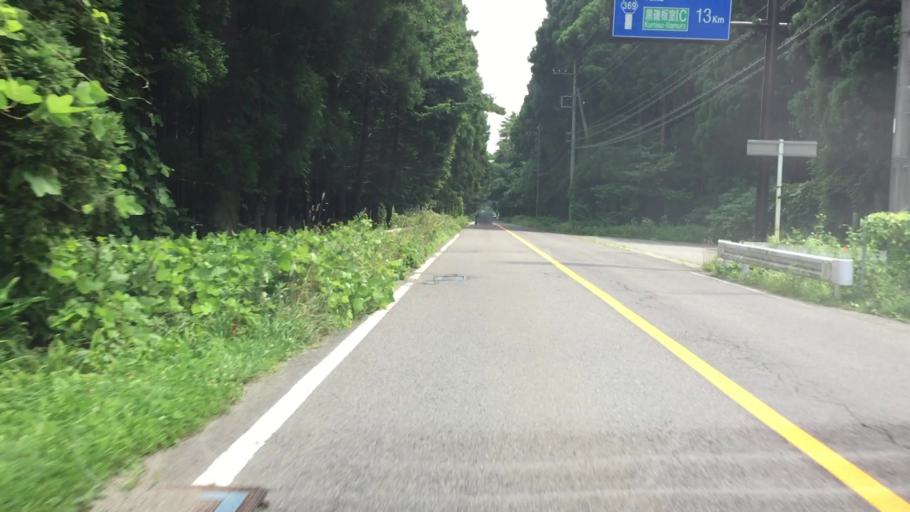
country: JP
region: Tochigi
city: Kuroiso
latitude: 37.0398
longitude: 139.9421
